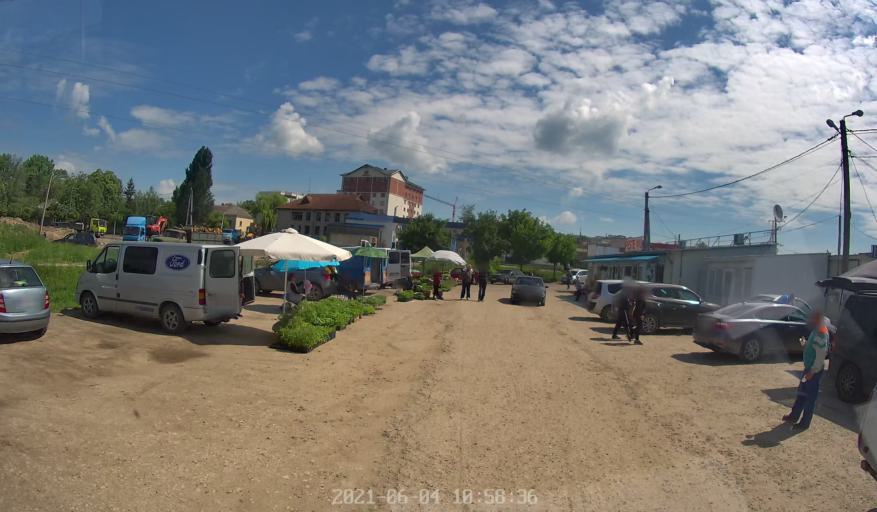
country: MD
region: Laloveni
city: Ialoveni
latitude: 46.9438
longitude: 28.7747
